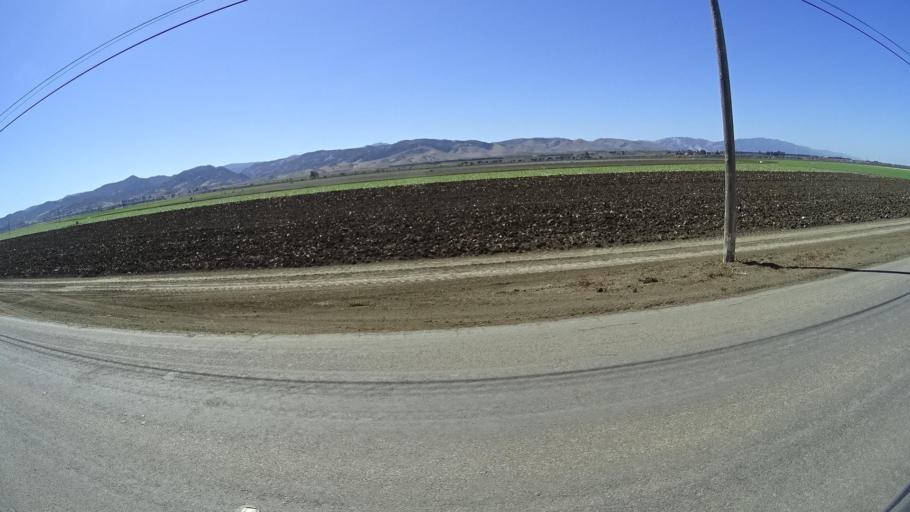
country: US
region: California
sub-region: Monterey County
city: King City
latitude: 36.2557
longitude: -121.1503
